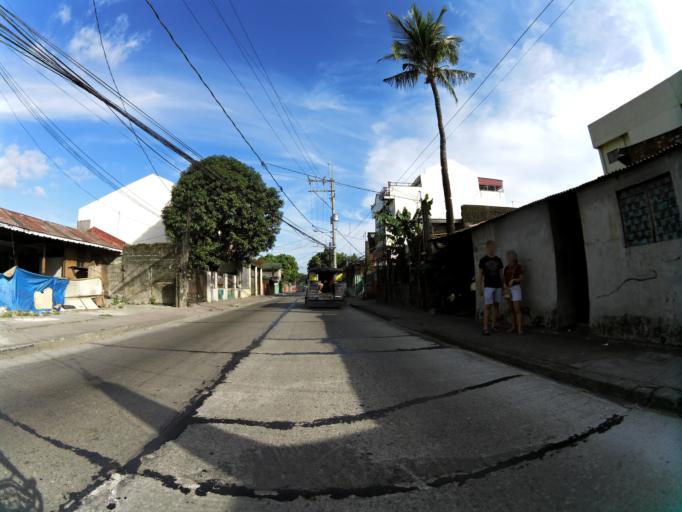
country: PH
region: Metro Manila
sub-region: Marikina
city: Calumpang
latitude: 14.6419
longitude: 121.1008
